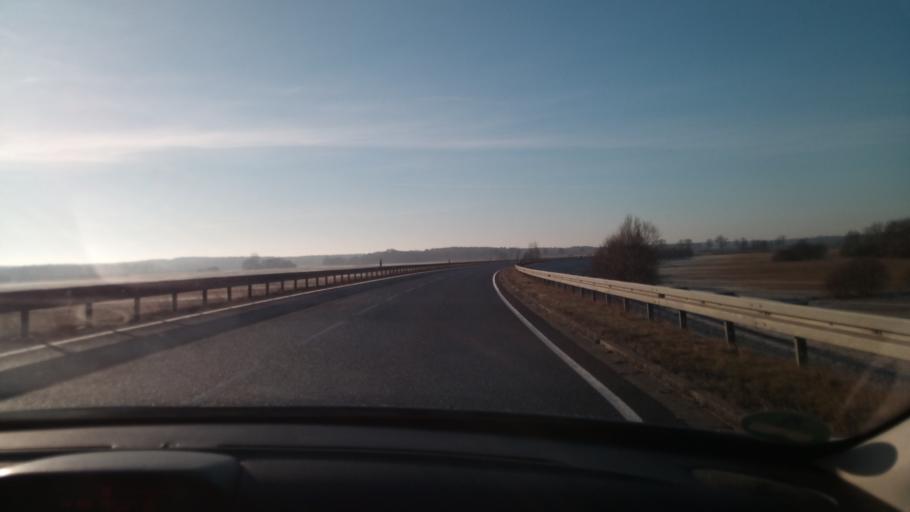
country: DE
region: Mecklenburg-Vorpommern
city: Neustrelitz
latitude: 53.3280
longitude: 13.1096
